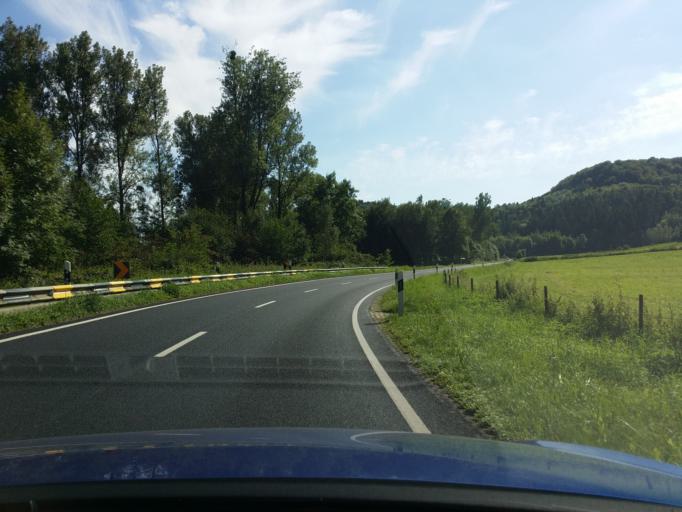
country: LU
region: Luxembourg
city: Rollingen
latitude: 49.7070
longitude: 6.0910
